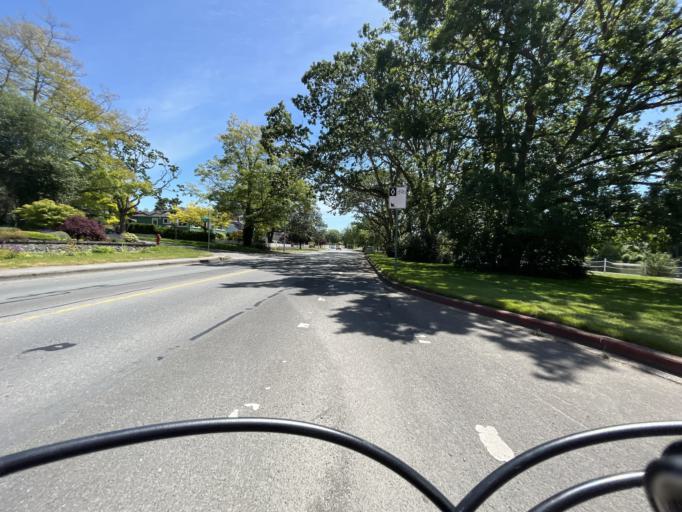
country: CA
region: British Columbia
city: Victoria
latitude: 48.4522
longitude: -123.4176
